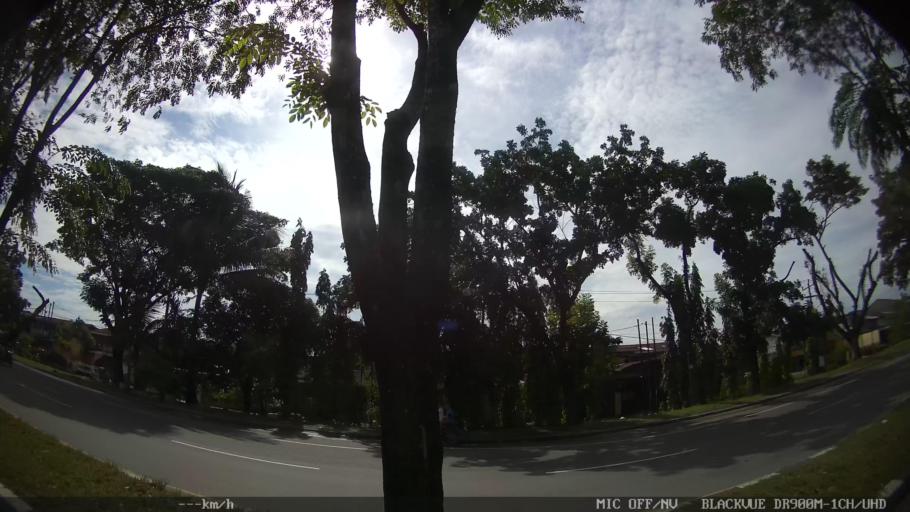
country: ID
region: North Sumatra
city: Sunggal
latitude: 3.6136
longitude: 98.6280
